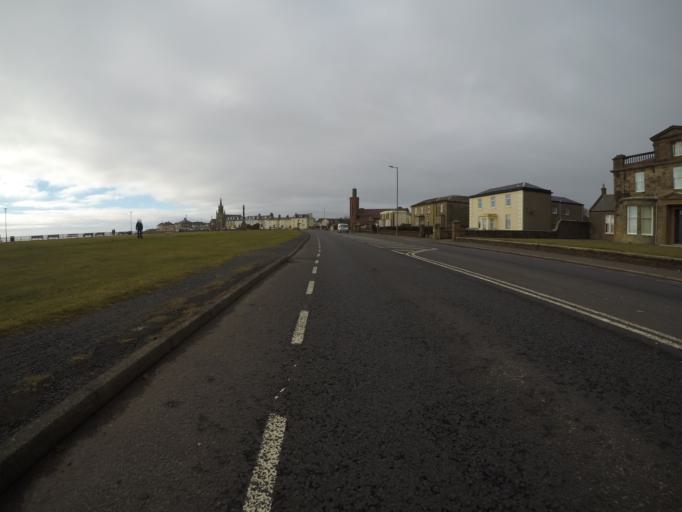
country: GB
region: Scotland
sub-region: North Ayrshire
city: Ardrossan
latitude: 55.6405
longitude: -4.8068
